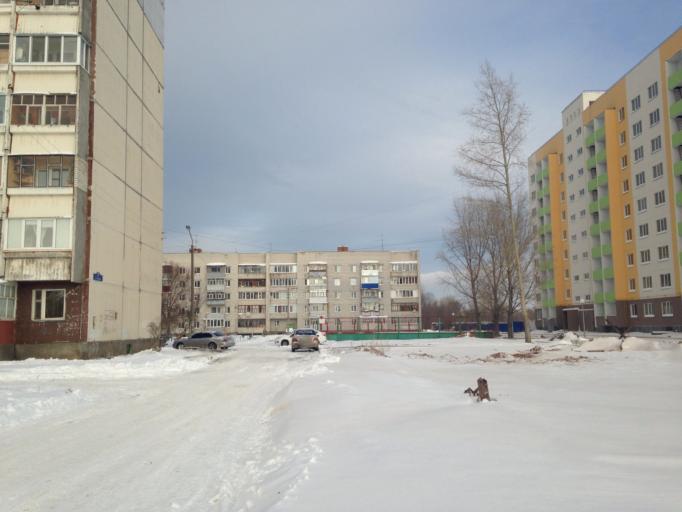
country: RU
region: Ulyanovsk
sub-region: Ulyanovskiy Rayon
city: Ulyanovsk
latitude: 54.3207
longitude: 48.4718
